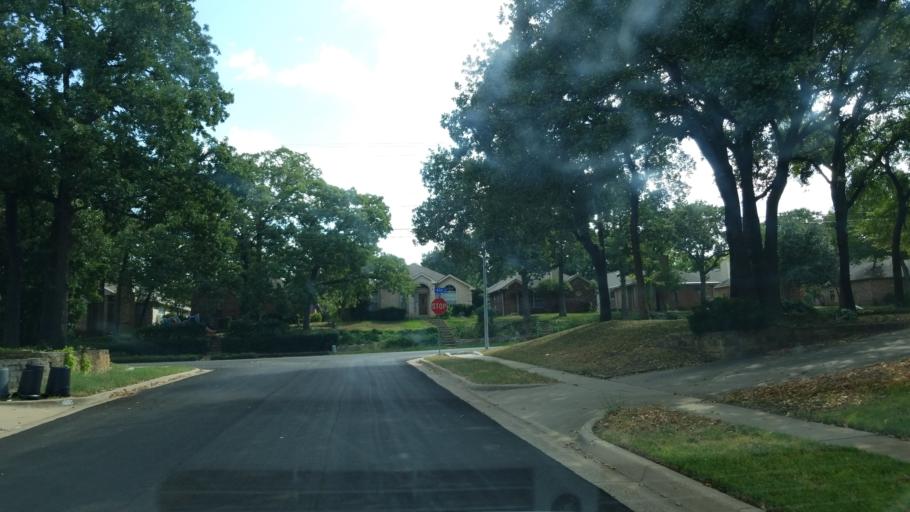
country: US
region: Texas
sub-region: Tarrant County
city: Euless
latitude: 32.8594
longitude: -97.0755
